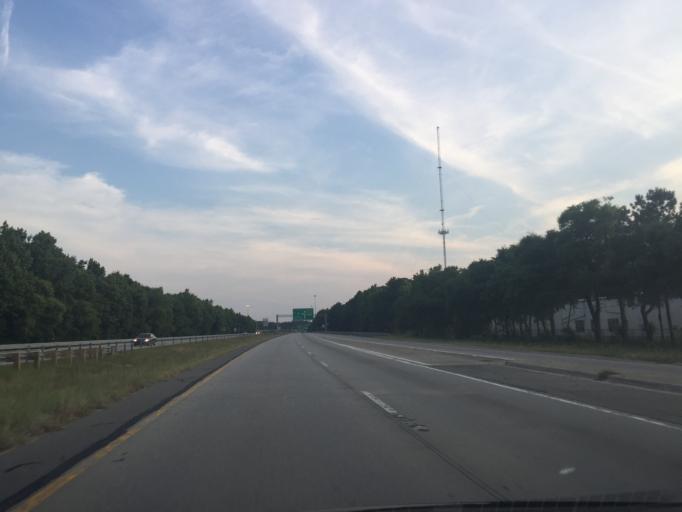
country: US
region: Georgia
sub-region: Chatham County
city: Savannah
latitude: 32.0512
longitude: -81.1429
